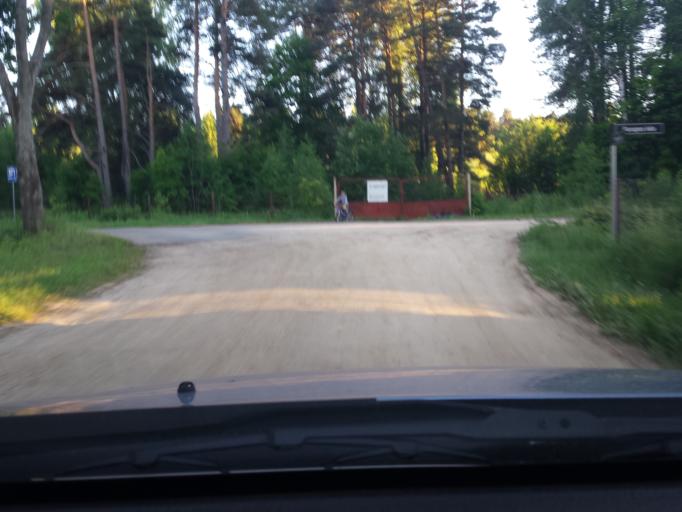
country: LV
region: Carnikava
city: Carnikava
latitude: 57.1166
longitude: 24.2344
